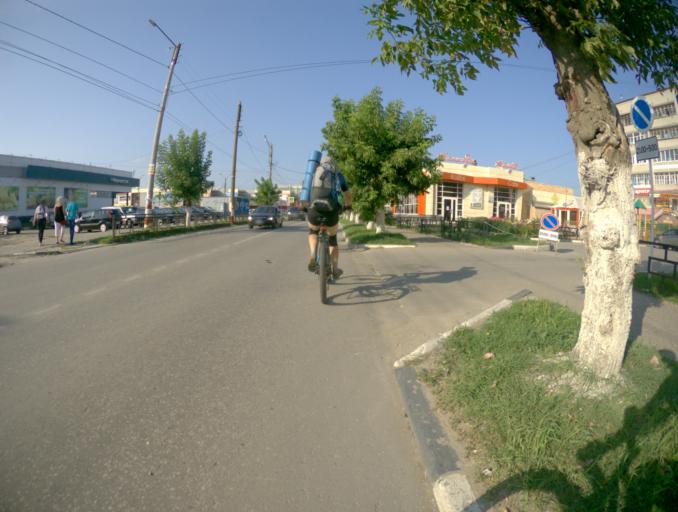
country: RU
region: Nizjnij Novgorod
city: Bor
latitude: 56.3593
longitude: 44.0534
